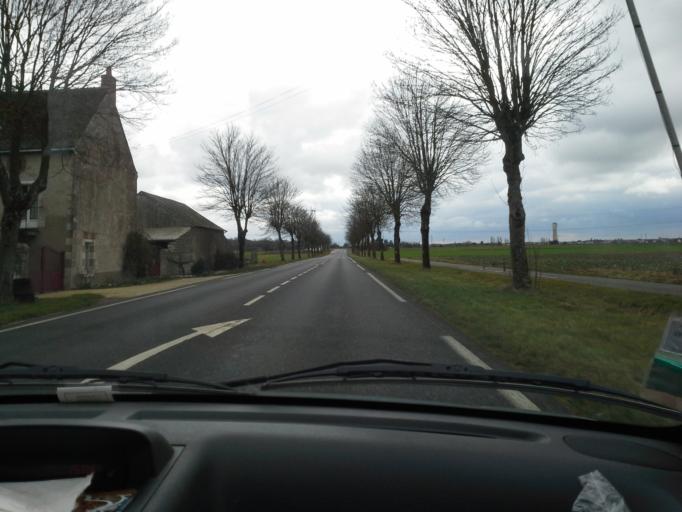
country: FR
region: Centre
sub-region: Departement du Loir-et-Cher
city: Saint-Sulpice-de-Pommeray
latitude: 47.6423
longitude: 1.2785
